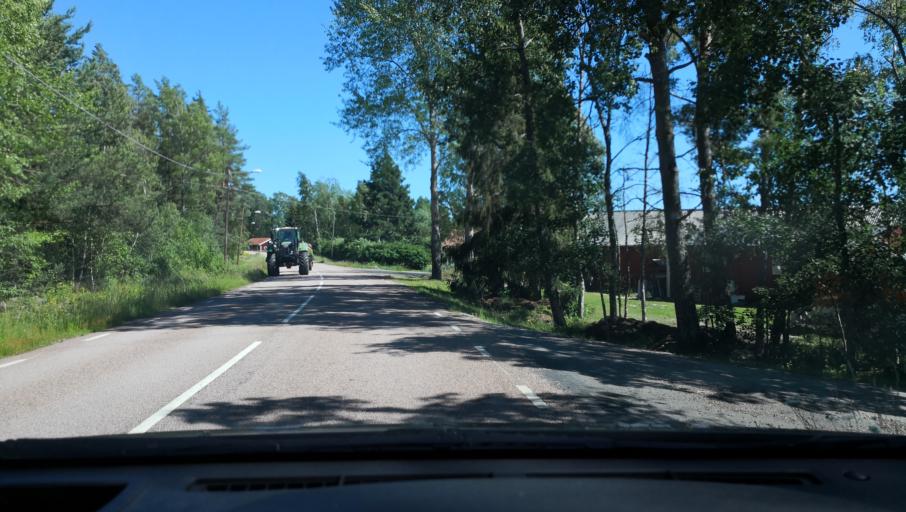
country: SE
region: Vaestmanland
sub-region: Arboga Kommun
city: Tyringe
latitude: 59.2948
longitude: 16.0383
